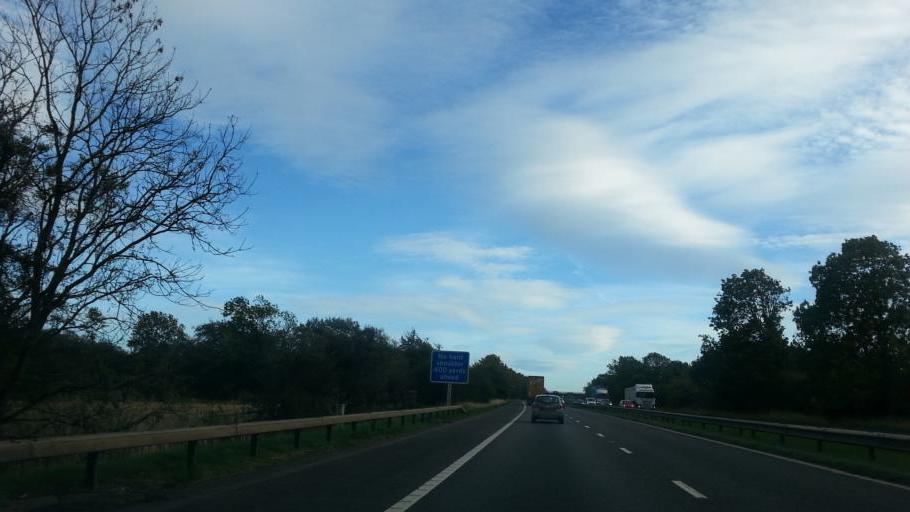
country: GB
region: England
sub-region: Doncaster
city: Stainton
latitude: 53.4705
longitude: -1.1384
